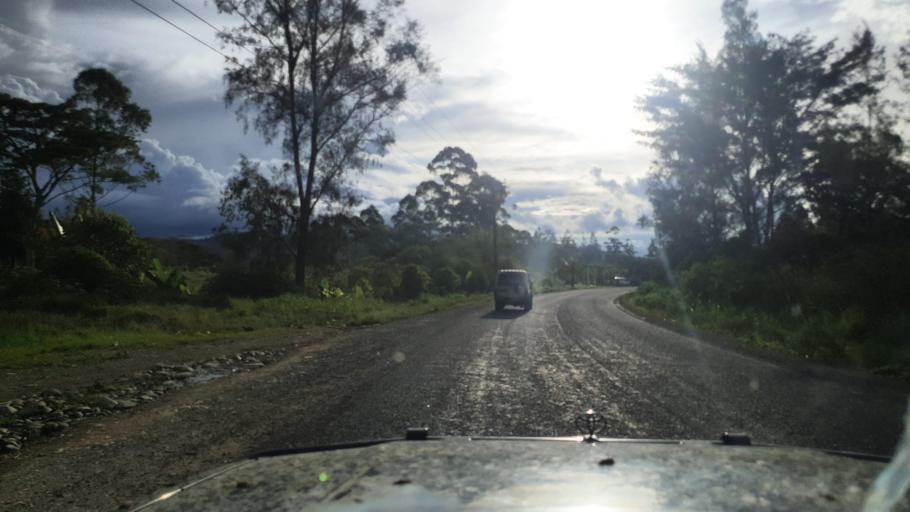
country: PG
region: Jiwaka
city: Minj
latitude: -5.8459
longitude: 144.5256
